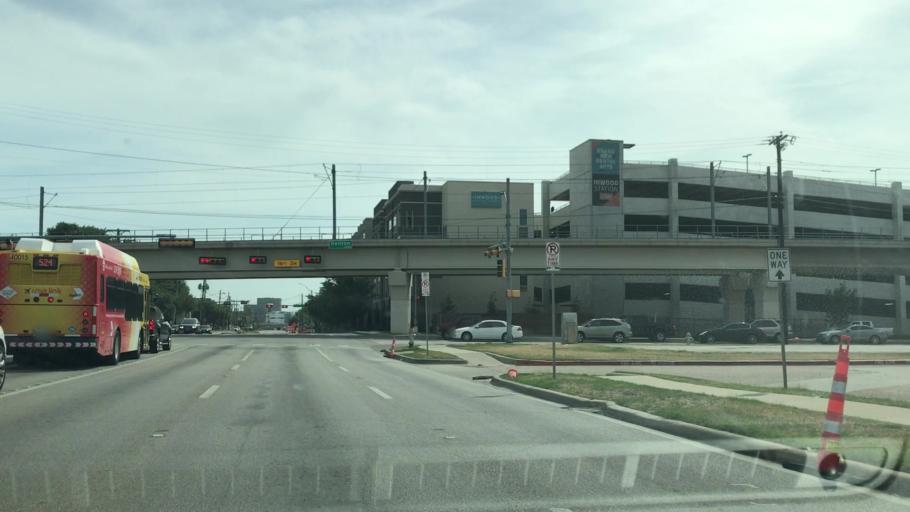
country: US
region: Texas
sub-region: Dallas County
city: University Park
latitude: 32.8240
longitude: -96.8333
